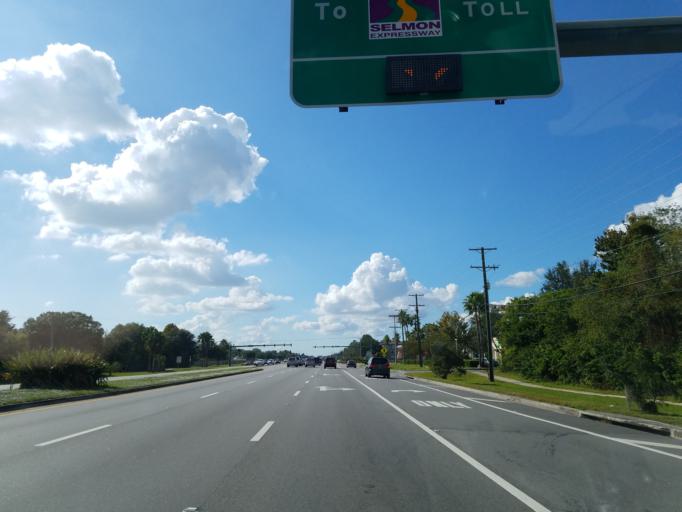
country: US
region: Florida
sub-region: Hillsborough County
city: Brandon
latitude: 27.9234
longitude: -82.3004
